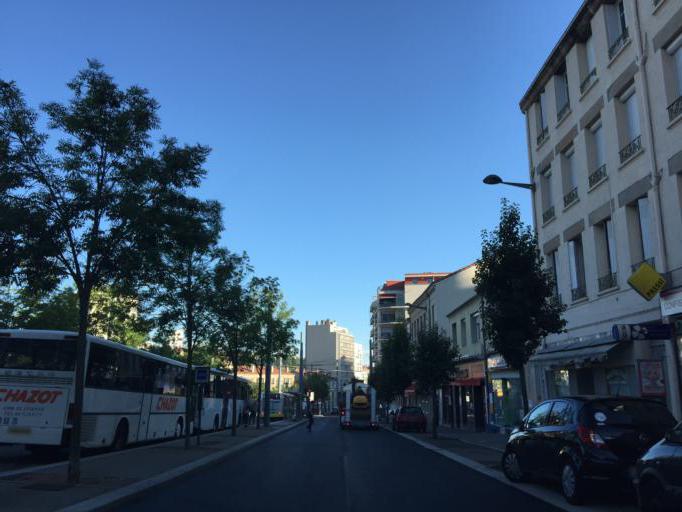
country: FR
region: Rhone-Alpes
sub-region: Departement de la Loire
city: Saint-Etienne
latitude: 45.4148
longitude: 4.3950
